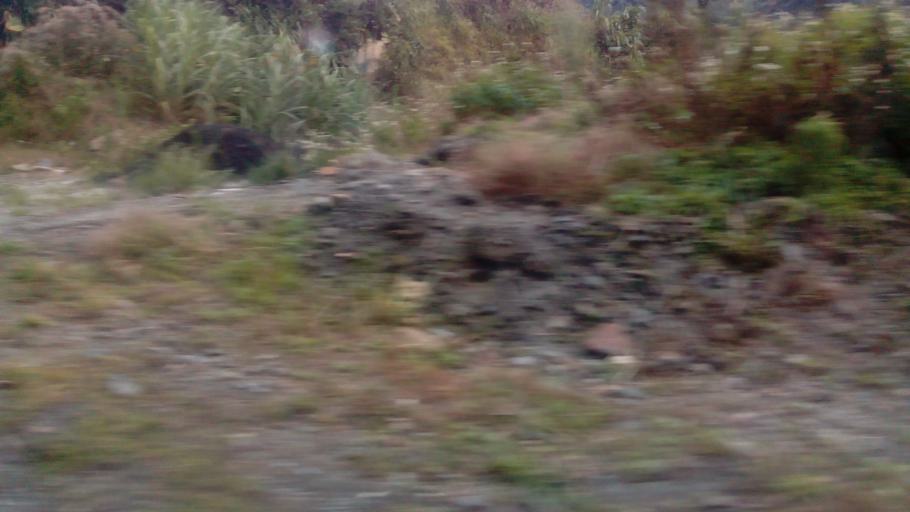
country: TW
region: Taiwan
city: Daxi
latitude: 24.4569
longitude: 121.3937
